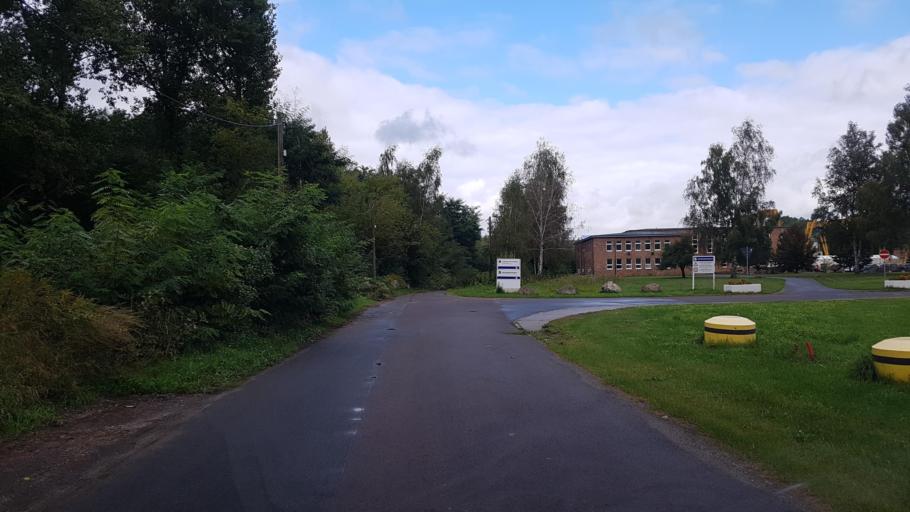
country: DE
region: Brandenburg
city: Lauchhammer
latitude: 51.4840
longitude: 13.7442
